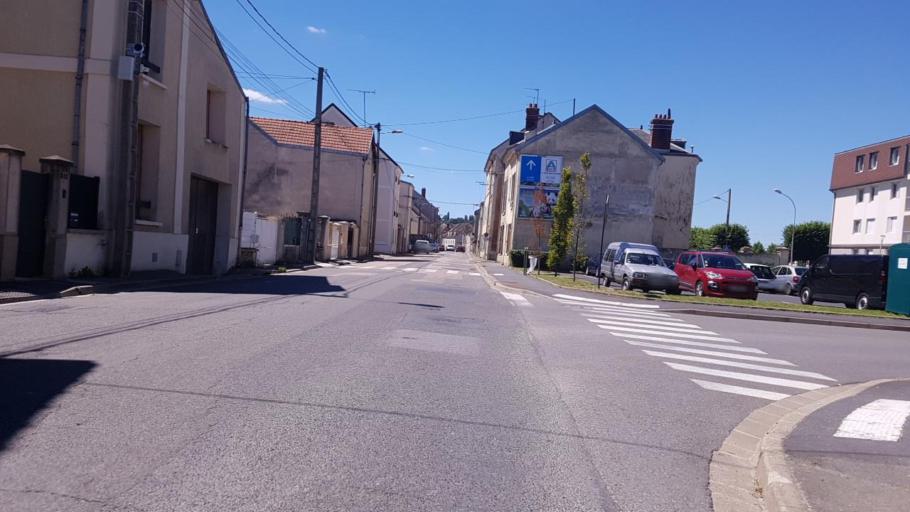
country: FR
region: Ile-de-France
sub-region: Departement de Seine-et-Marne
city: La Ferte-sous-Jouarre
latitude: 48.9502
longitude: 3.1360
